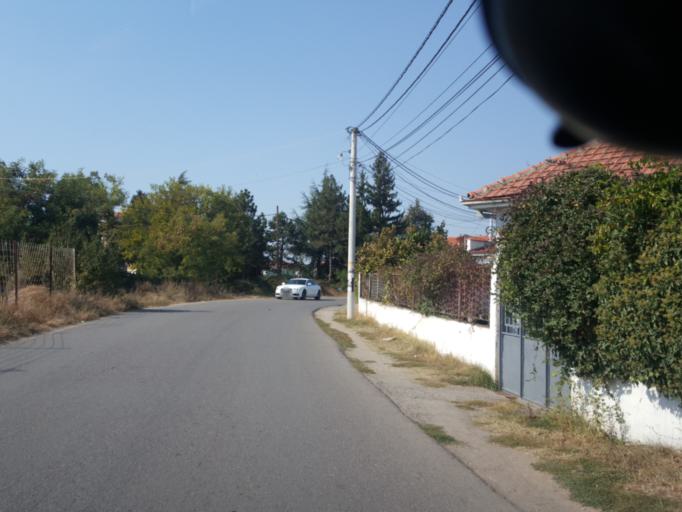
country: XK
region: Gjakova
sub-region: Komuna e Gjakoves
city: Gjakove
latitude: 42.3912
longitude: 20.4297
